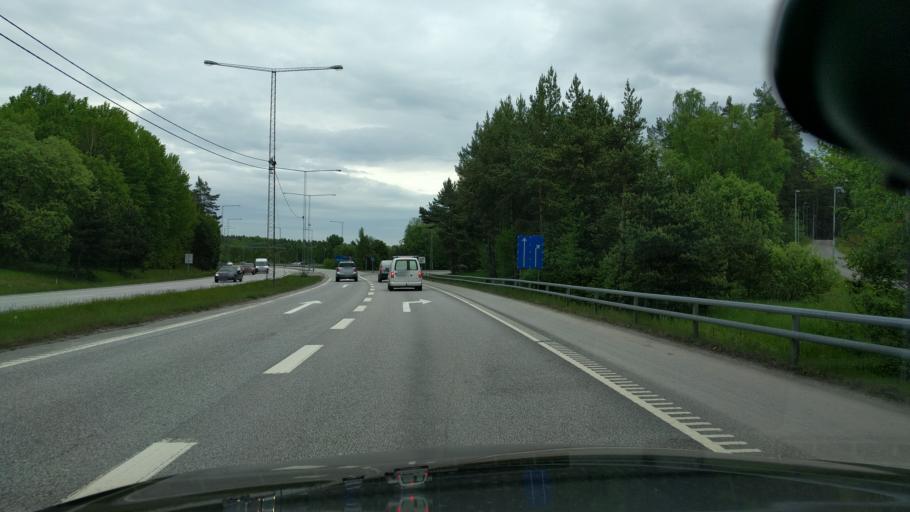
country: SE
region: Stockholm
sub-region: Taby Kommun
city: Taby
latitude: 59.4576
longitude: 18.1324
